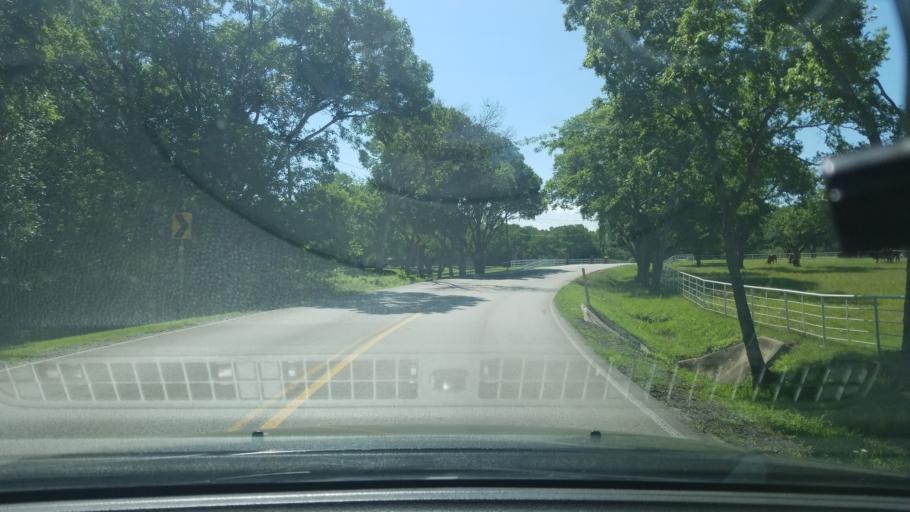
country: US
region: Texas
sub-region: Dallas County
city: Sunnyvale
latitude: 32.7960
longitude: -96.5699
